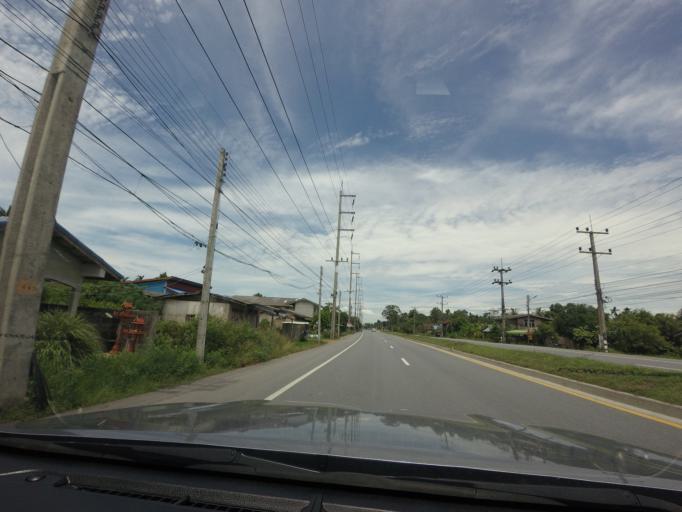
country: TH
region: Songkhla
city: Krasae Sin
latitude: 7.6157
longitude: 100.3973
